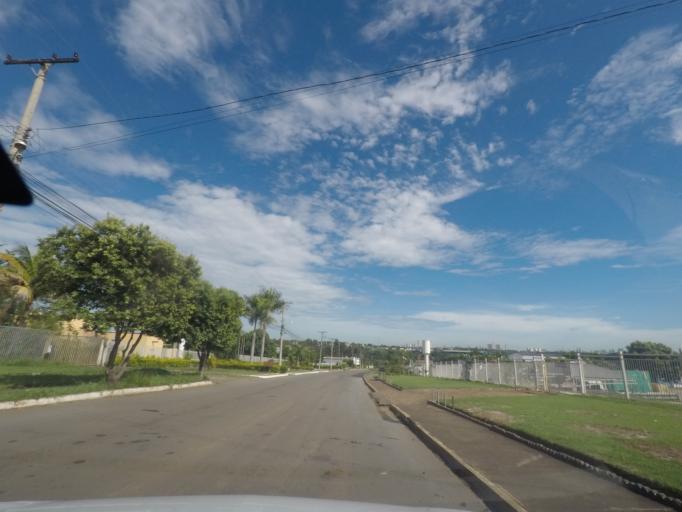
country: BR
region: Goias
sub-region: Aparecida De Goiania
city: Aparecida de Goiania
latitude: -16.7951
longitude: -49.2608
